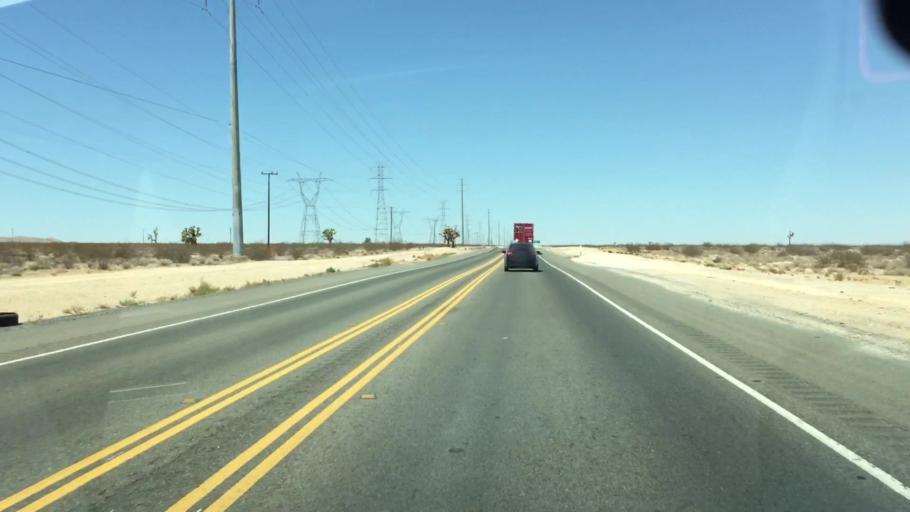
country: US
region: California
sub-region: San Bernardino County
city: Adelanto
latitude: 34.7070
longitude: -117.4557
